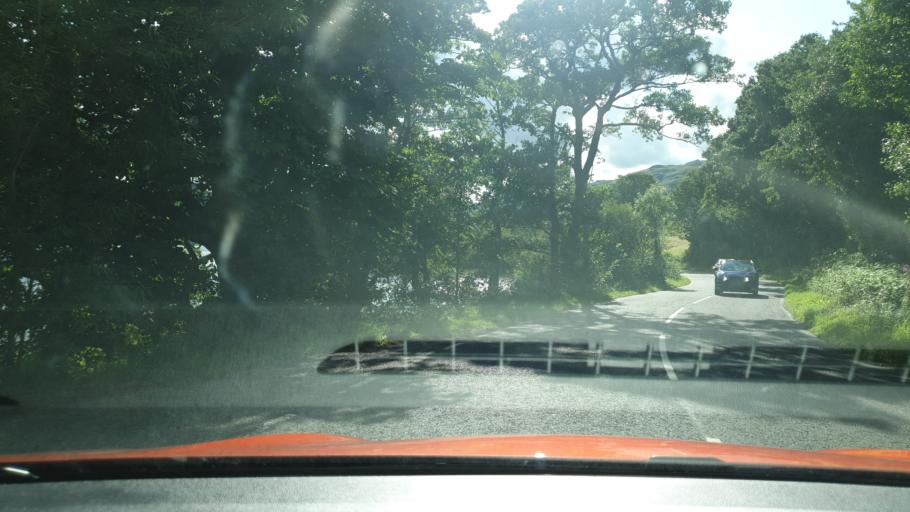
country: GB
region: England
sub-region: Cumbria
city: Penrith
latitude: 54.5819
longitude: -2.8771
